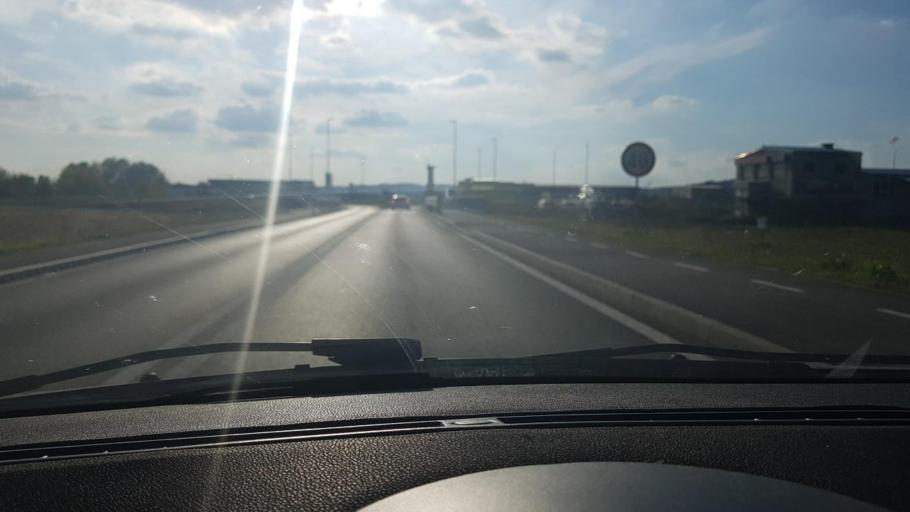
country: HR
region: Krapinsko-Zagorska
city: Zabok
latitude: 46.0157
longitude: 15.8874
